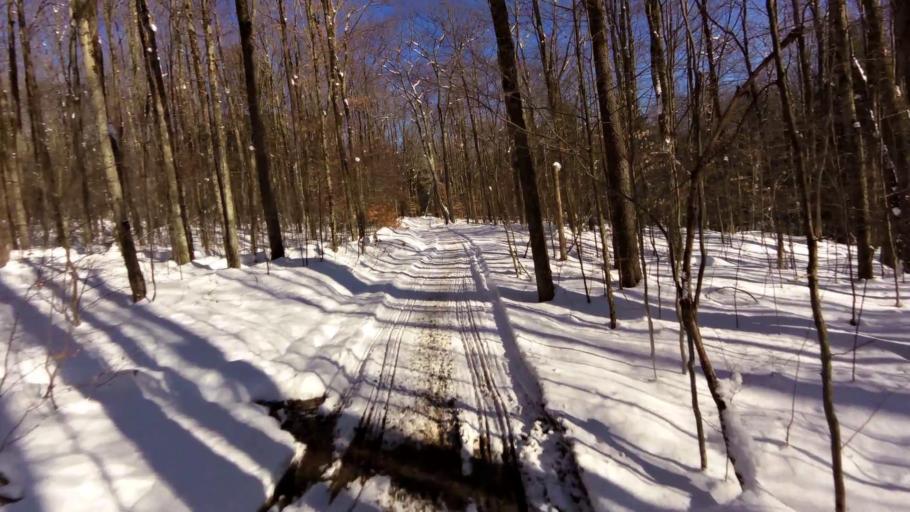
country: US
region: New York
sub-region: Cattaraugus County
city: Salamanca
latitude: 42.0223
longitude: -78.7882
